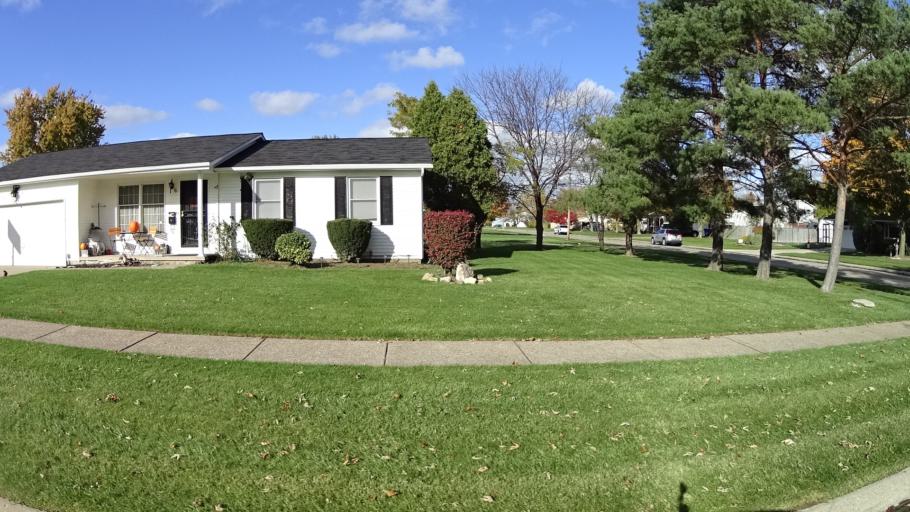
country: US
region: Ohio
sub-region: Lorain County
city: Lorain
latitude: 41.4361
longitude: -82.2012
